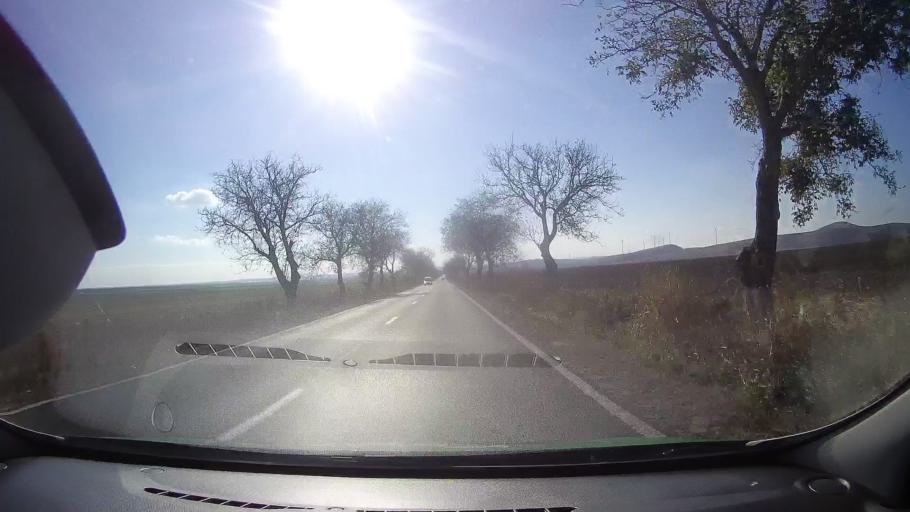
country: RO
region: Tulcea
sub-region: Comuna Ceamurlia de Jos
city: Ceamurlia de Jos
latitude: 44.8001
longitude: 28.6905
